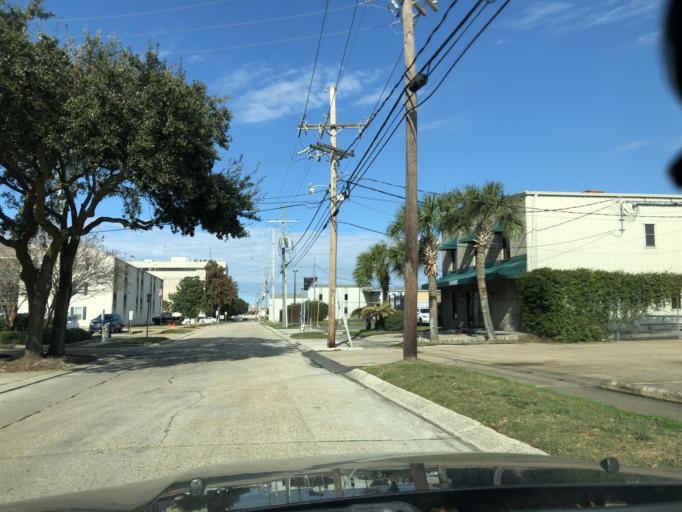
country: US
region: Louisiana
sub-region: Jefferson Parish
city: Metairie
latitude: 29.9947
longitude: -90.1624
